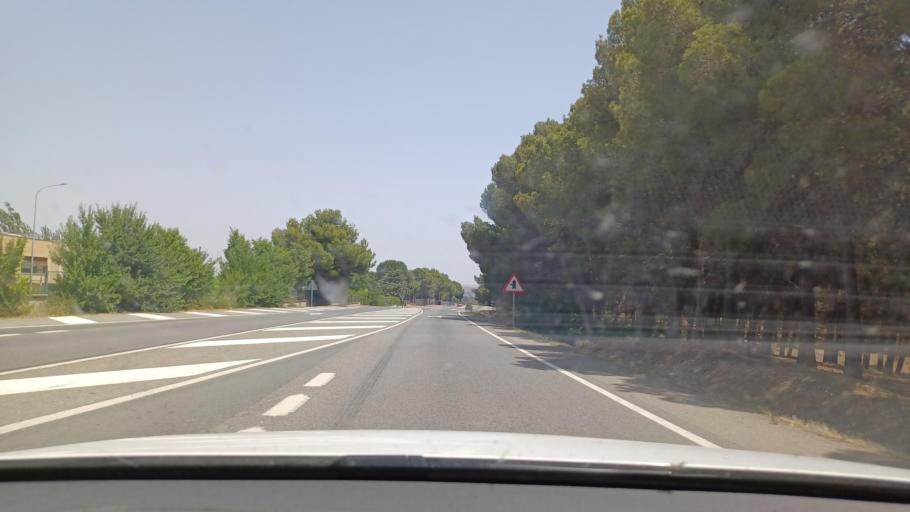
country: ES
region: Navarre
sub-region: Provincia de Navarra
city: Tudela
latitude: 42.0399
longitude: -1.6252
